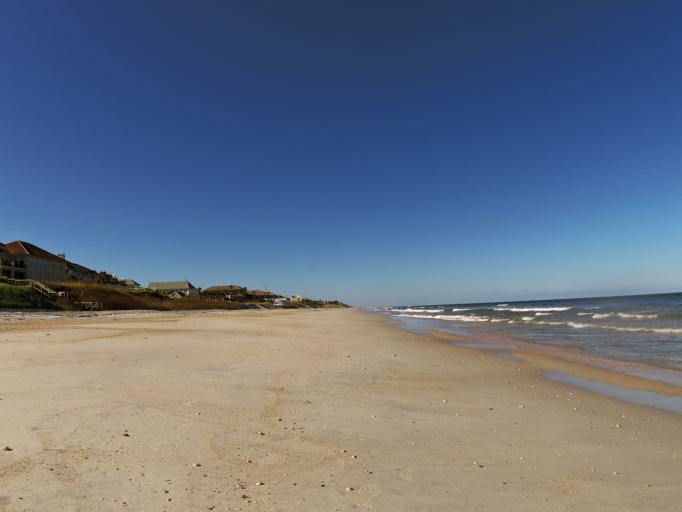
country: US
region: Florida
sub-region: Saint Johns County
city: Sawgrass
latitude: 30.1697
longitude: -81.3577
